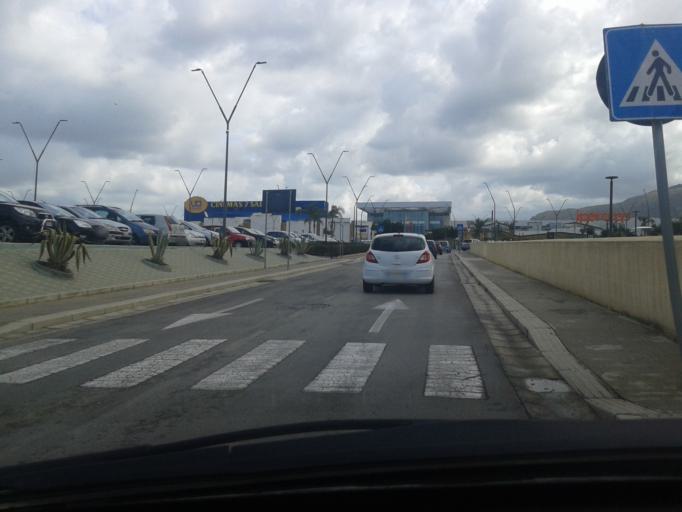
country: IT
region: Sicily
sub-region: Palermo
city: Ciaculli
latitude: 38.0907
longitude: 13.4103
